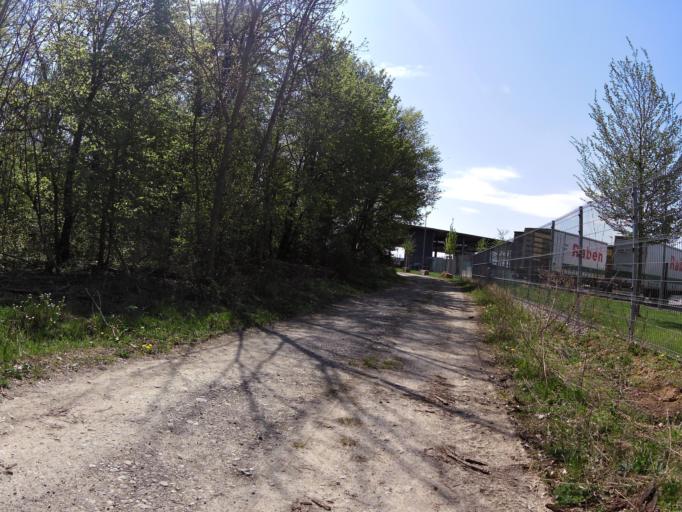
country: DE
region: Bavaria
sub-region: Regierungsbezirk Unterfranken
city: Giebelstadt
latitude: 49.6905
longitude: 9.9468
